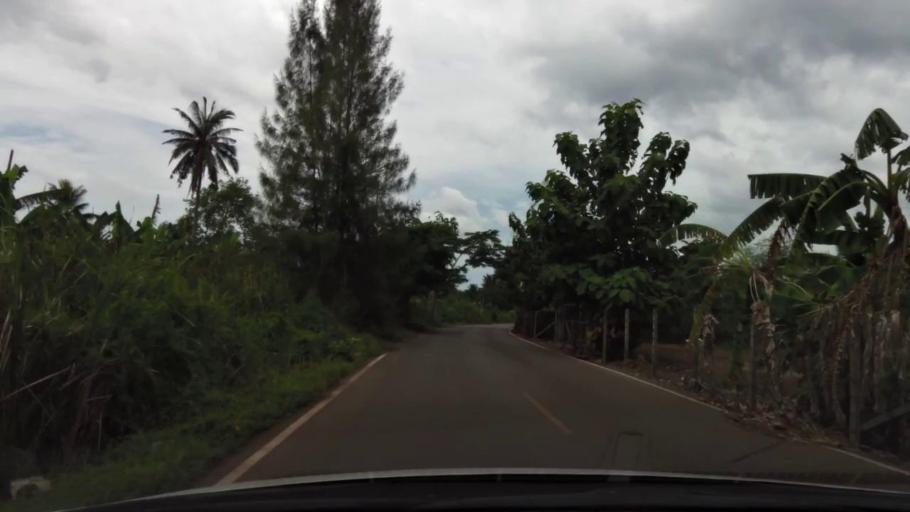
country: TH
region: Samut Sakhon
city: Ban Phaeo
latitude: 13.5639
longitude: 100.0338
